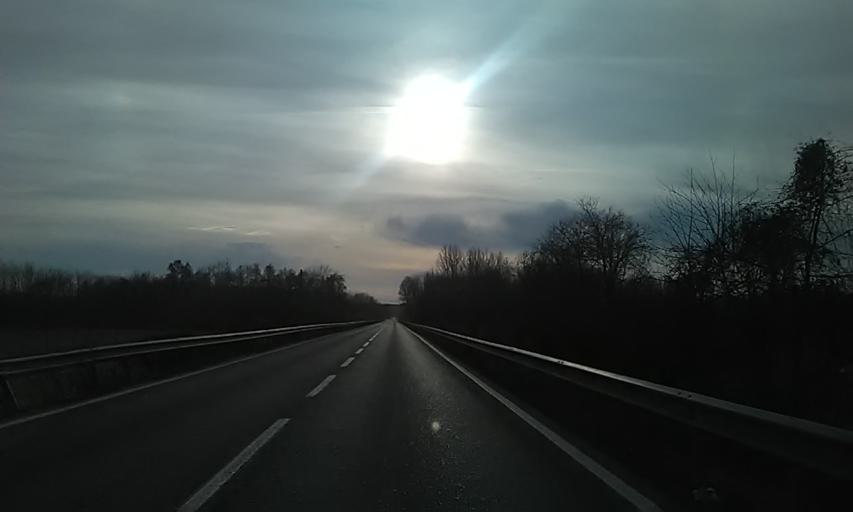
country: IT
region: Piedmont
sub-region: Provincia di Torino
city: Rondissone
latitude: 45.2601
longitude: 7.9727
